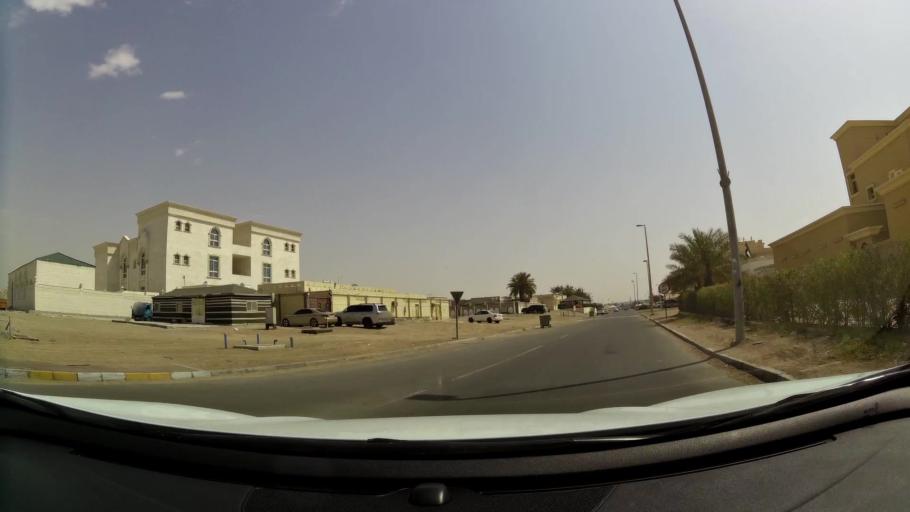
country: AE
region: Abu Dhabi
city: Abu Dhabi
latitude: 24.2965
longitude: 54.6456
